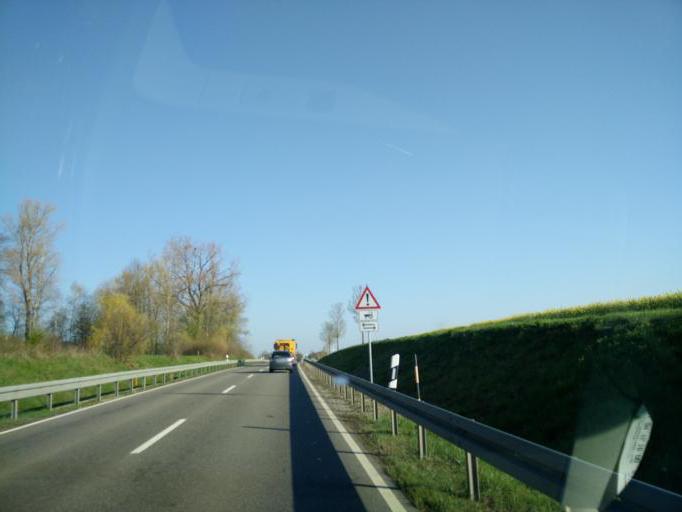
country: DE
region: Baden-Wuerttemberg
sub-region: Regierungsbezirk Stuttgart
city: Deckenpfronn
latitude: 48.6401
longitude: 8.8244
